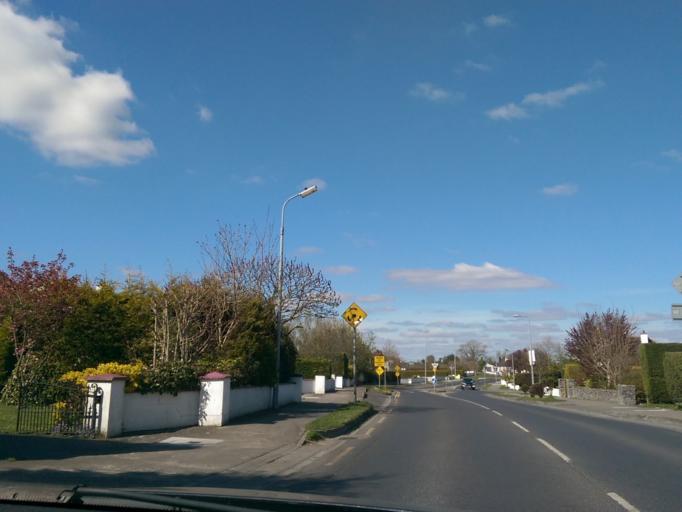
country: IE
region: Leinster
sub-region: Laois
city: Portlaoise
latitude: 53.0415
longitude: -7.2886
